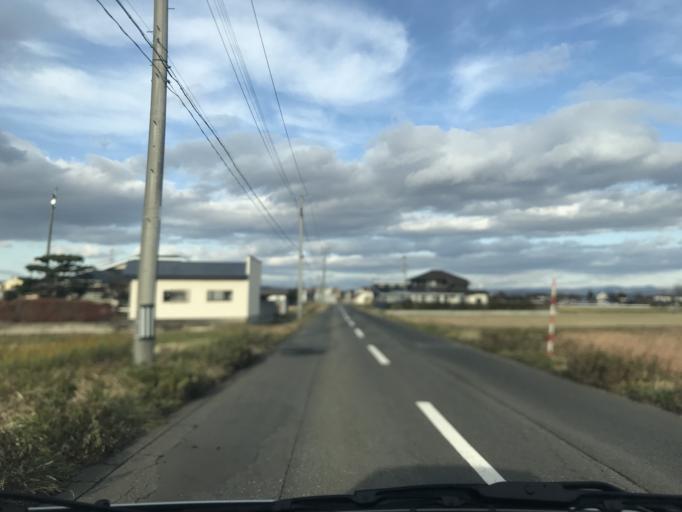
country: JP
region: Iwate
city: Mizusawa
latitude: 39.1879
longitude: 141.1065
